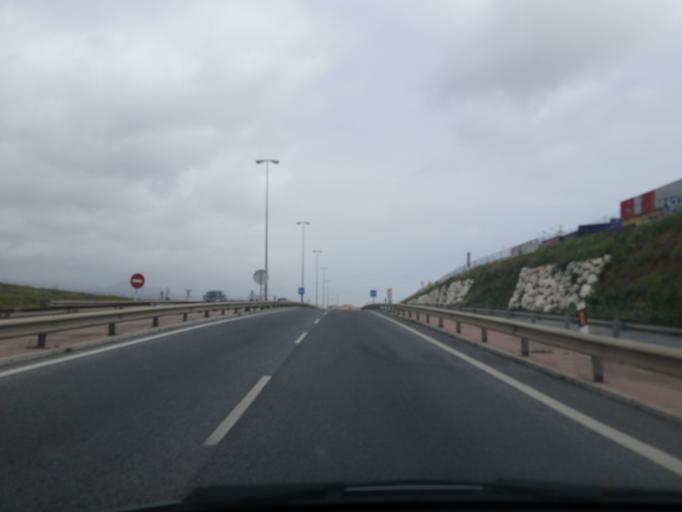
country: ES
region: Andalusia
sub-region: Provincia de Malaga
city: Malaga
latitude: 36.7140
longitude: -4.4883
